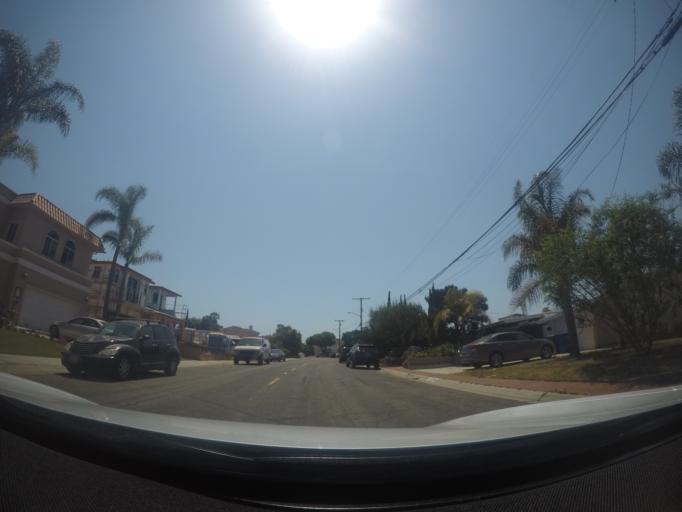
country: US
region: California
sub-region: Los Angeles County
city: Palos Verdes Estates
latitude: 33.8174
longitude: -118.3680
